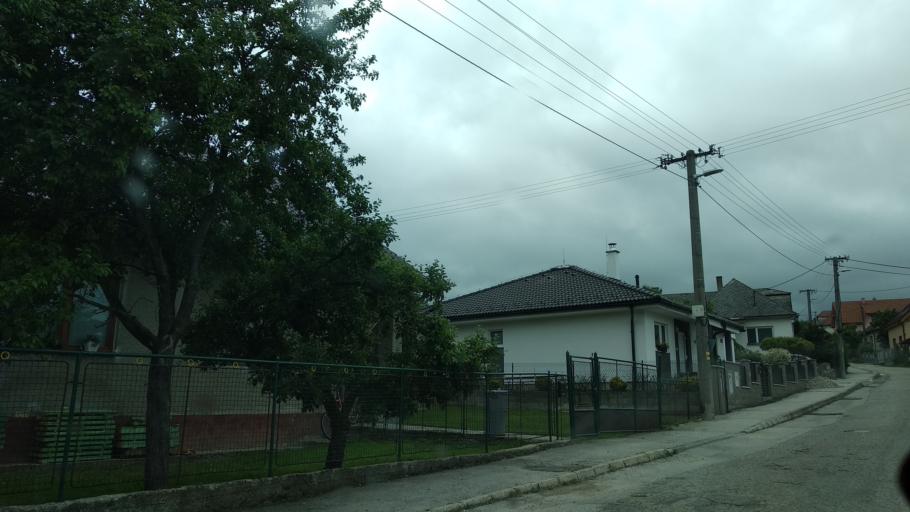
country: SK
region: Trenciansky
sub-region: Okres Trencin
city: Trencin
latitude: 48.8004
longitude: 18.1108
